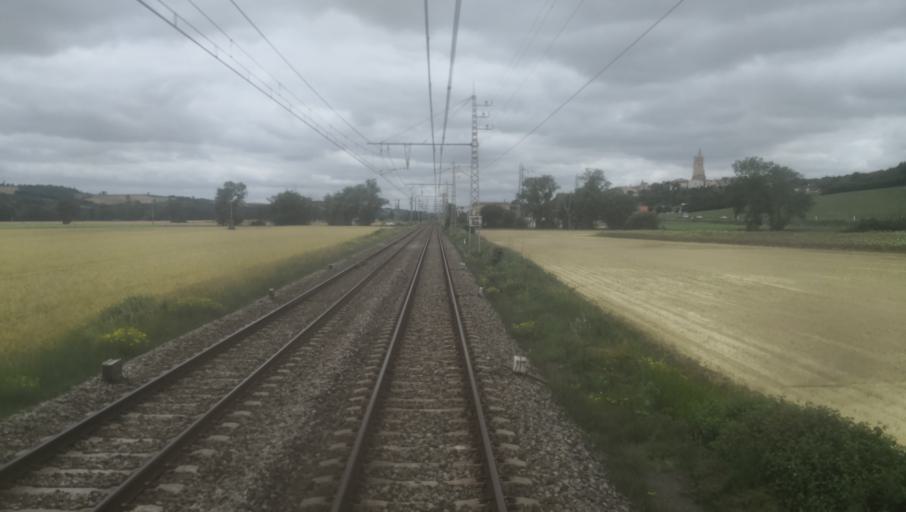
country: FR
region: Midi-Pyrenees
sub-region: Departement de la Haute-Garonne
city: Avignonet-Lauragais
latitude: 43.3614
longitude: 1.7971
